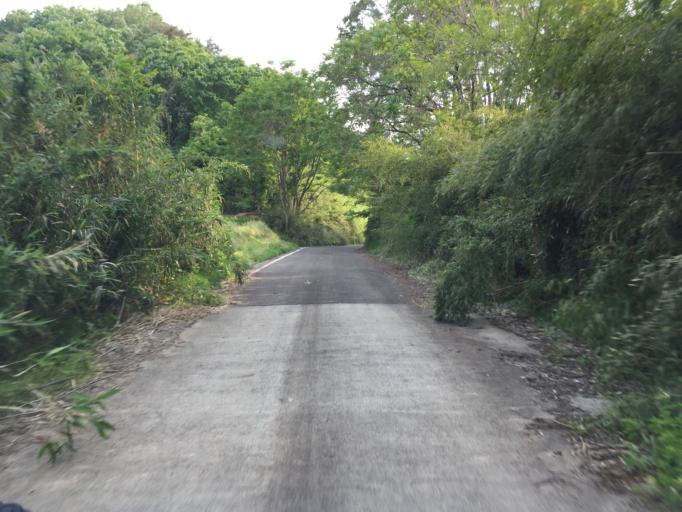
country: JP
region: Fukushima
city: Fukushima-shi
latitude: 37.7010
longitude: 140.4288
